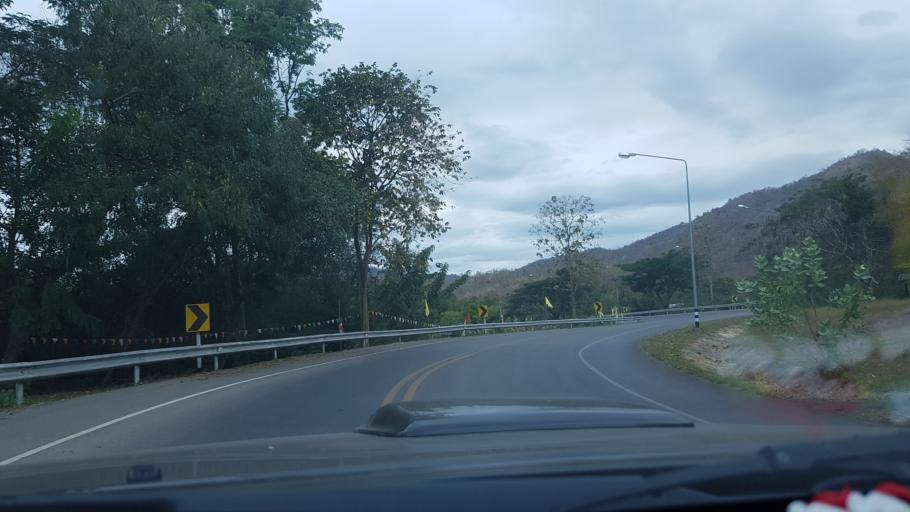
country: TH
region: Phetchabun
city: Phetchabun
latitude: 16.5321
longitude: 101.1007
